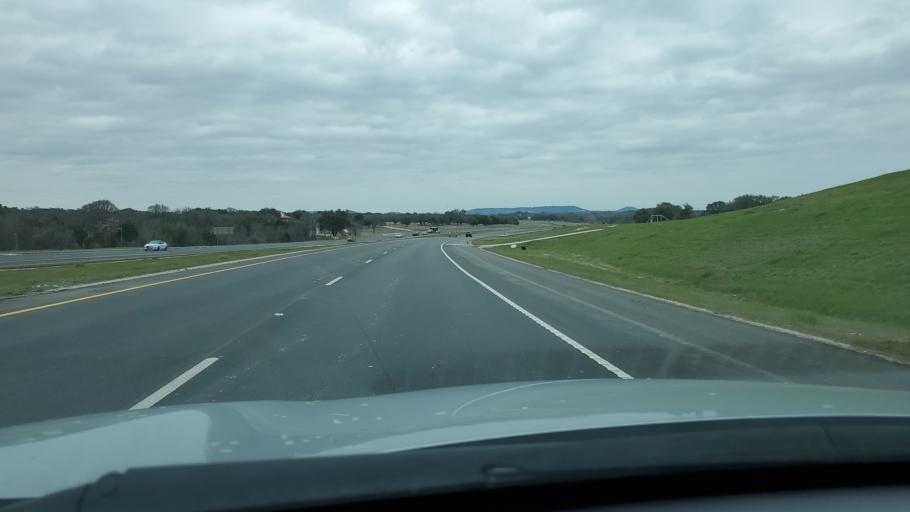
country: US
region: Texas
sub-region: Williamson County
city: Florence
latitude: 30.9355
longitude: -97.7912
